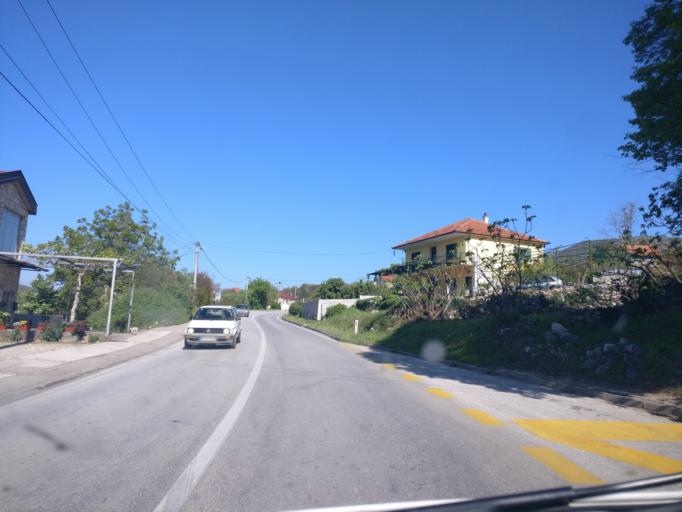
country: BA
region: Federation of Bosnia and Herzegovina
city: Capljina
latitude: 43.1397
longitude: 17.6678
